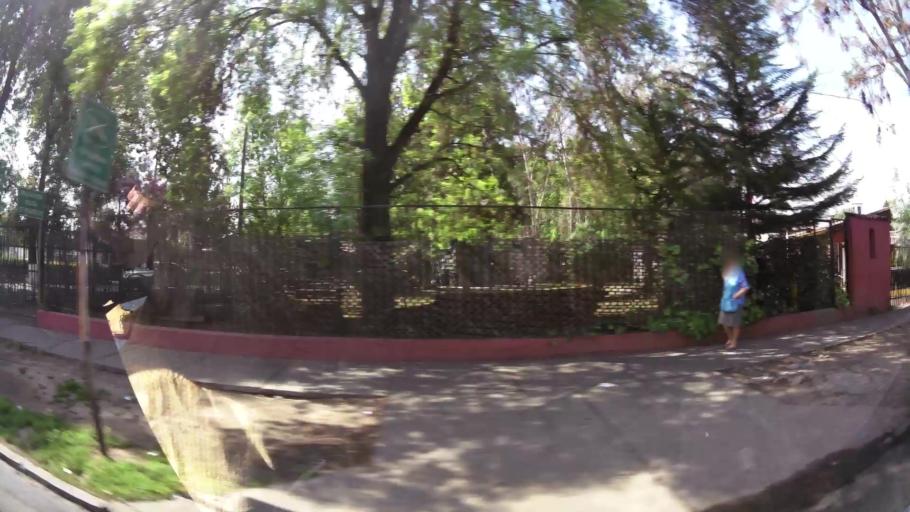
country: CL
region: Santiago Metropolitan
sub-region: Provincia de Santiago
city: Lo Prado
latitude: -33.4216
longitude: -70.6959
